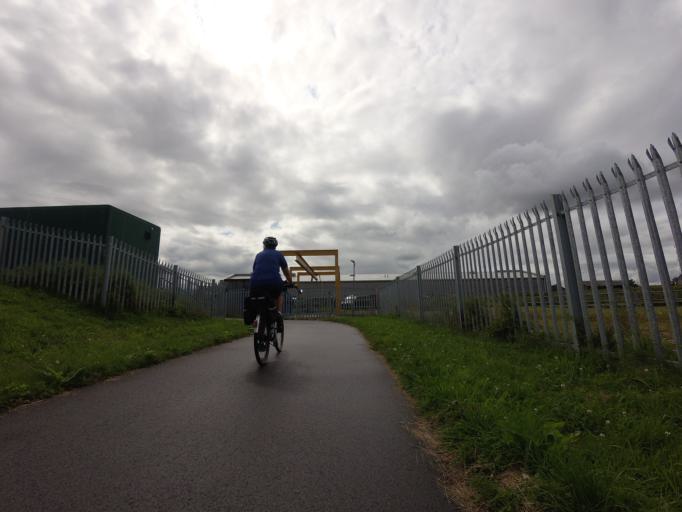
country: GB
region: Scotland
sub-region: Moray
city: Elgin
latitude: 57.6517
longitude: -3.2921
